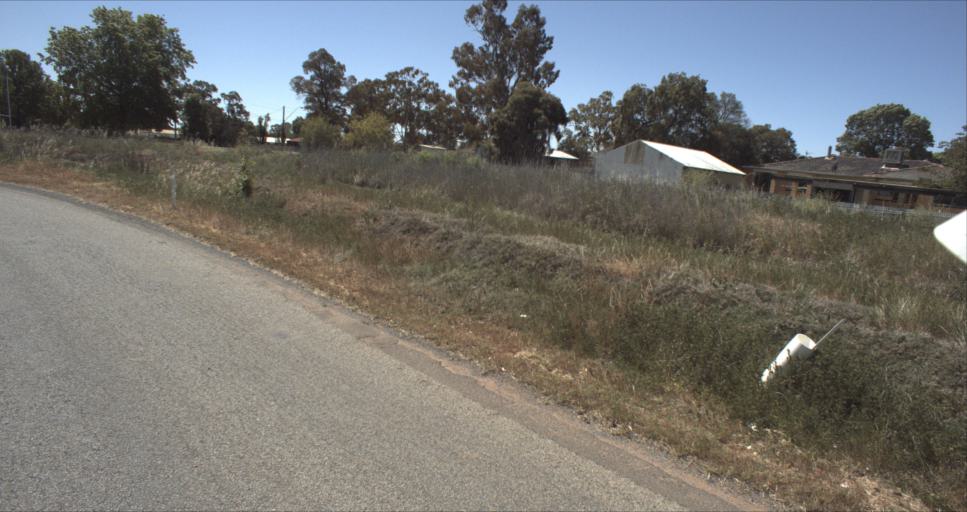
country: AU
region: New South Wales
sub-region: Leeton
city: Leeton
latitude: -34.5496
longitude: 146.3724
